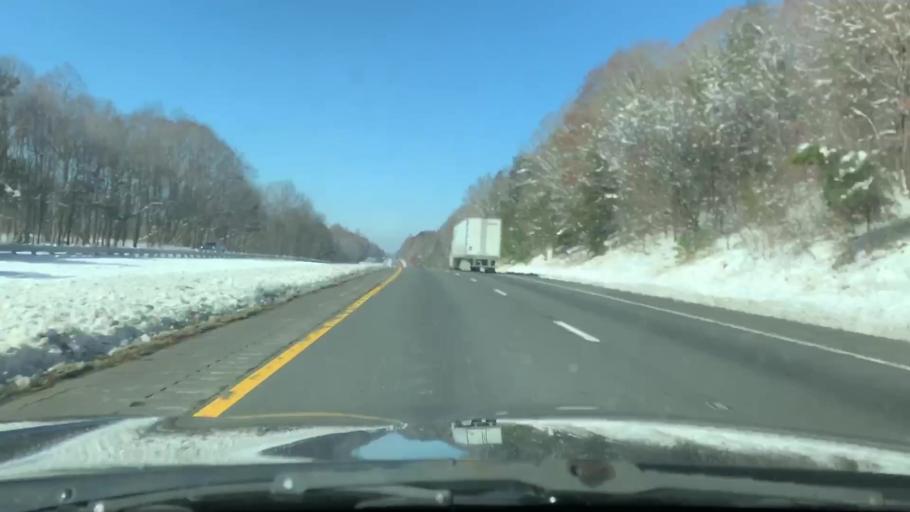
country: US
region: North Carolina
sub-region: Orange County
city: Hillsborough
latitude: 36.0469
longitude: -79.0473
